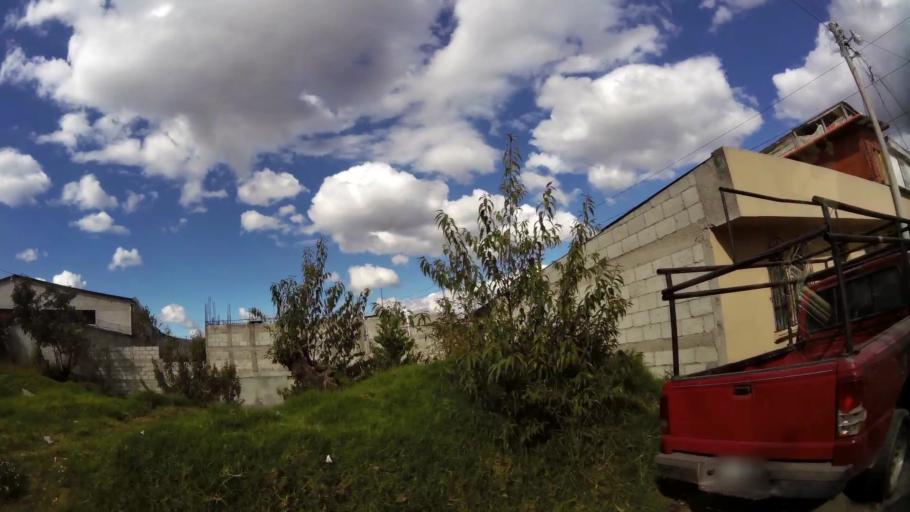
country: GT
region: Quetzaltenango
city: Quetzaltenango
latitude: 14.8311
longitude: -91.5375
